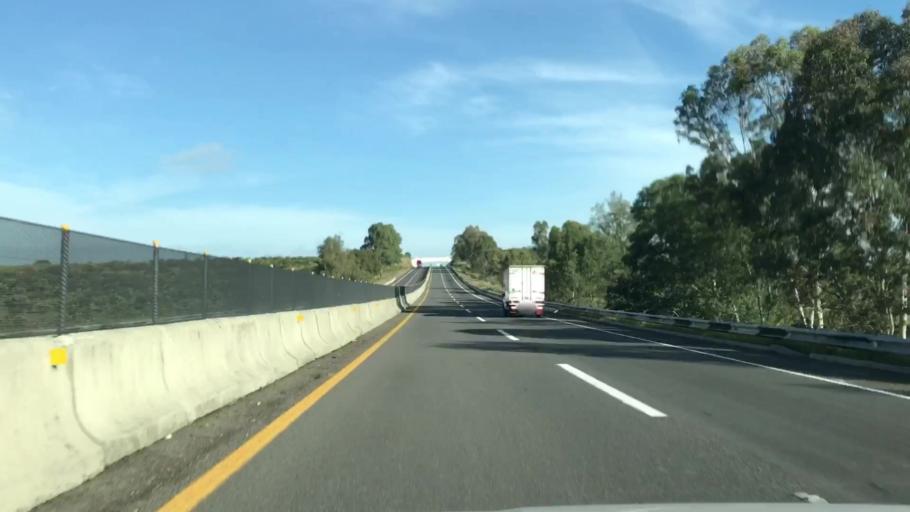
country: MX
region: Jalisco
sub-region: Lagos de Moreno
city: Cristeros [Fraccionamiento]
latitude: 21.3789
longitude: -102.1377
